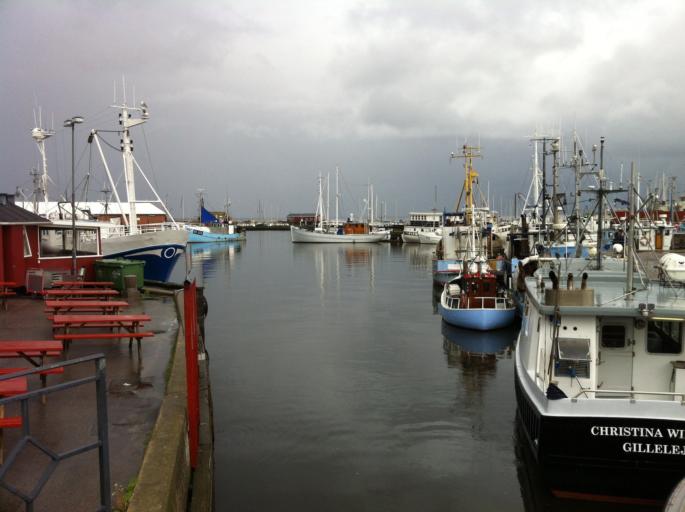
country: DK
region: Capital Region
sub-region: Gribskov Kommune
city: Gilleleje
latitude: 56.1264
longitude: 12.3084
